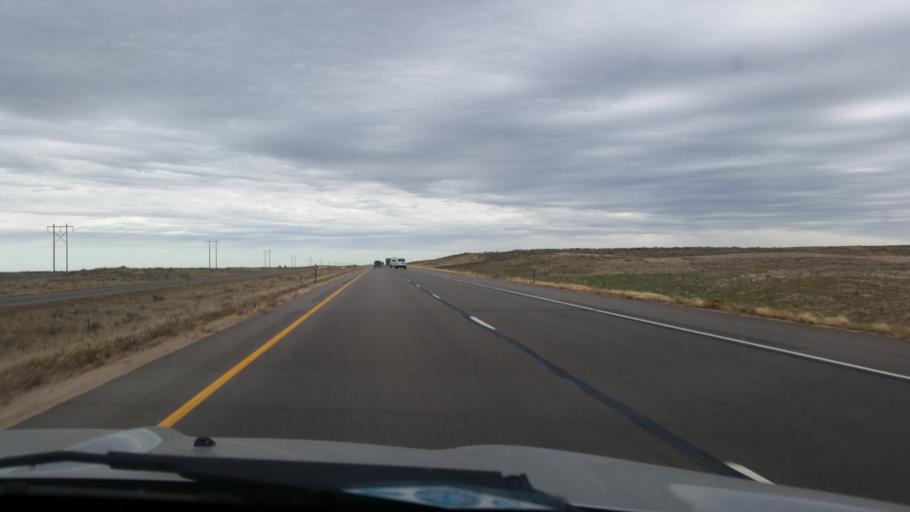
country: US
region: Colorado
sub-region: Morgan County
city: Brush
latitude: 40.3440
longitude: -103.4540
